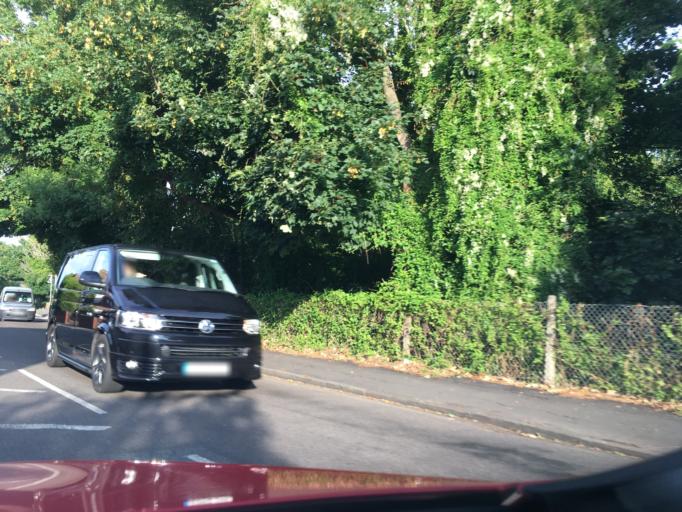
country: GB
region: England
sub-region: Bristol
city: Bristol
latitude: 51.4923
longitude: -2.6382
